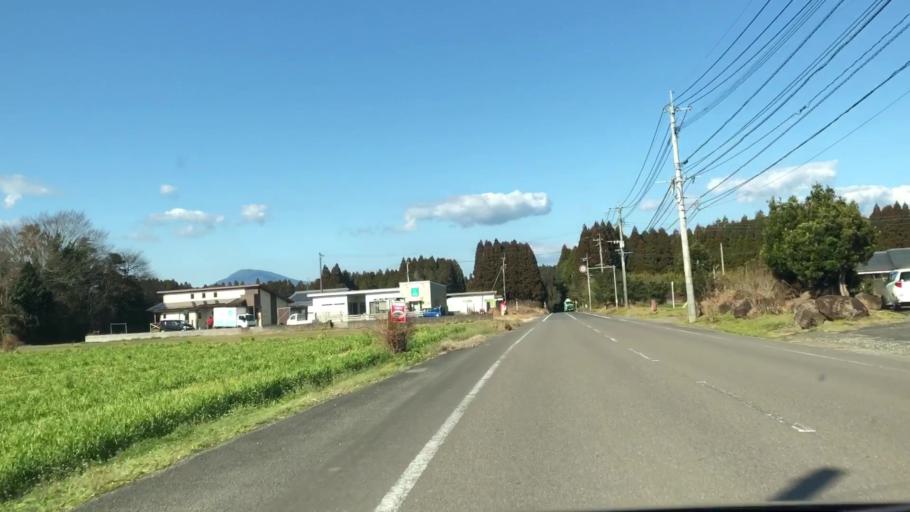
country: JP
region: Kagoshima
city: Satsumasendai
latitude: 31.8382
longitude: 130.4299
